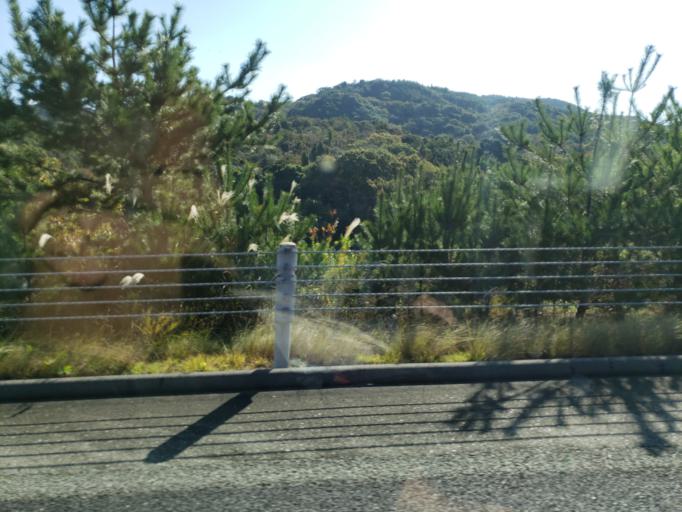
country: JP
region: Hyogo
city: Fukura
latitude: 34.2847
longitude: 134.7114
